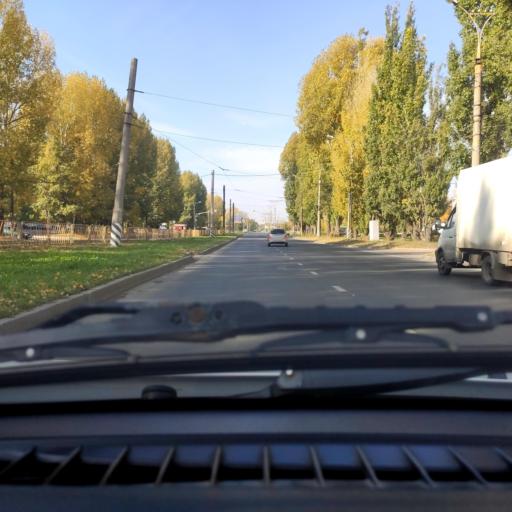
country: RU
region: Samara
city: Tol'yatti
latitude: 53.5113
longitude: 49.4594
